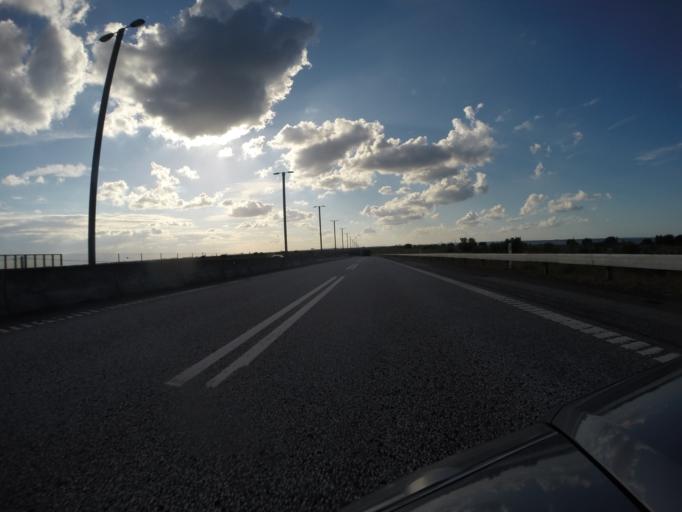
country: DK
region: Capital Region
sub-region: Dragor Kommune
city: Dragor
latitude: 55.6082
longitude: 12.7338
